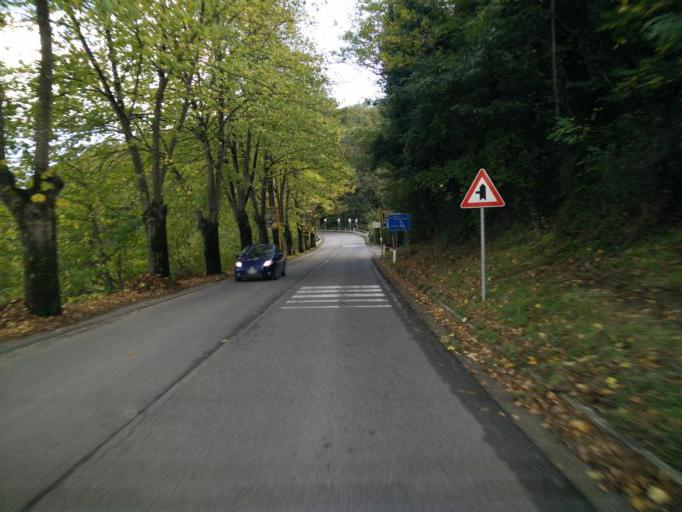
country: IT
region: Tuscany
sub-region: Province of Florence
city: Greve in Chianti
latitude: 43.5704
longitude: 11.3203
